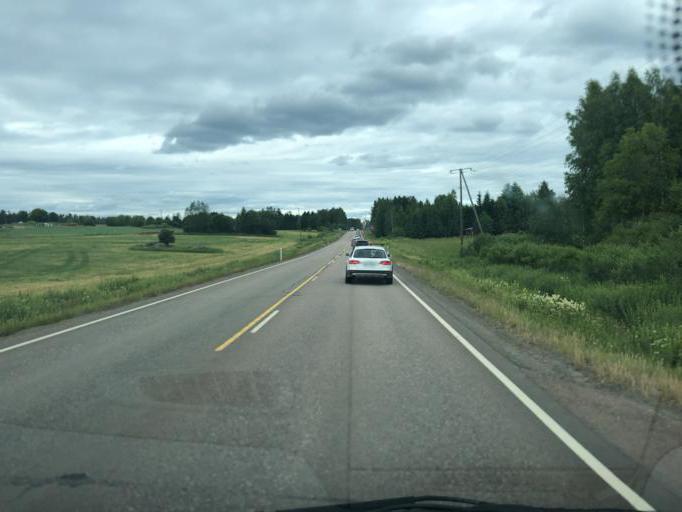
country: FI
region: Southern Savonia
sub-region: Mikkeli
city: Maentyharju
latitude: 61.0834
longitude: 27.0639
